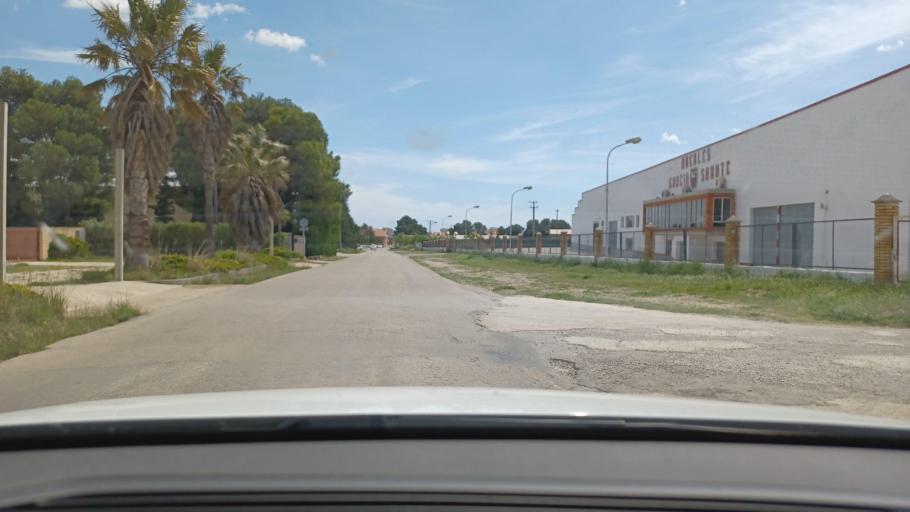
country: ES
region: Valencia
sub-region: Provincia de Castello
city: Rosell
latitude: 40.6424
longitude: 0.2752
